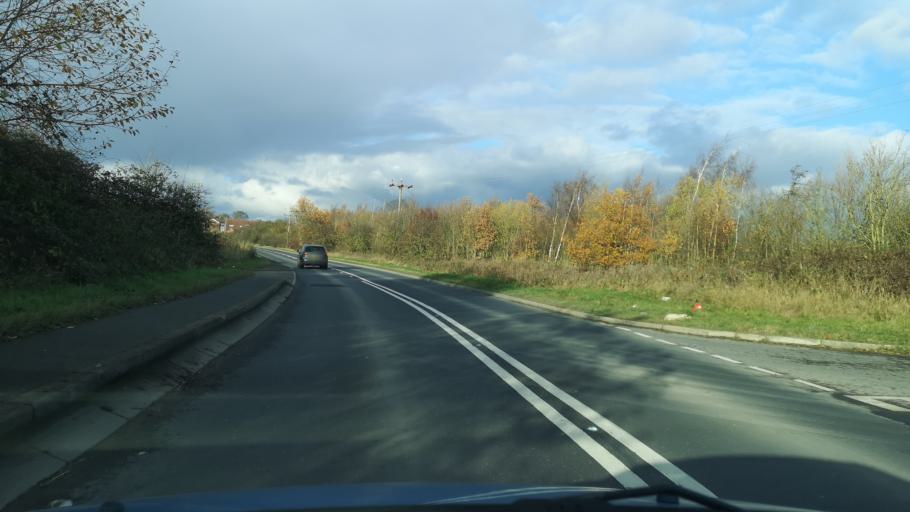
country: GB
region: England
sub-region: City and Borough of Wakefield
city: Featherstone
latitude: 53.6871
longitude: -1.3754
